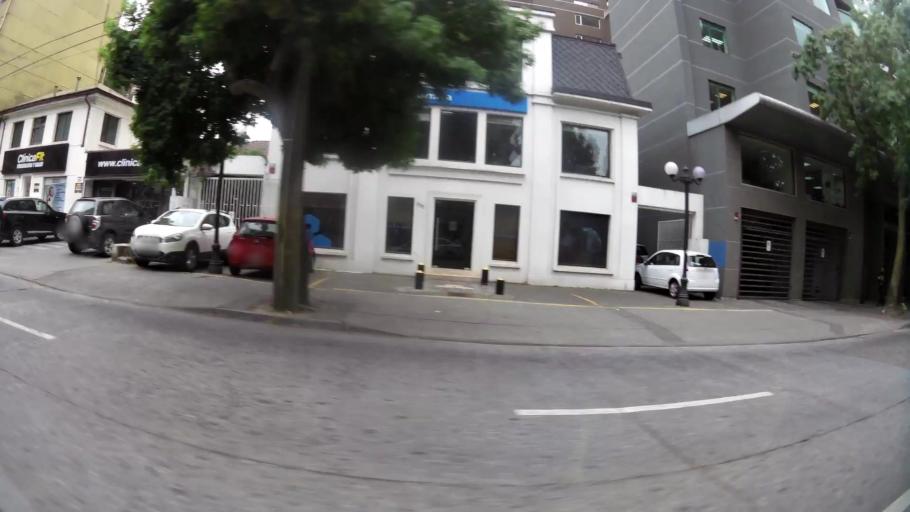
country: CL
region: Biobio
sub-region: Provincia de Concepcion
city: Concepcion
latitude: -36.8285
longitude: -73.0430
